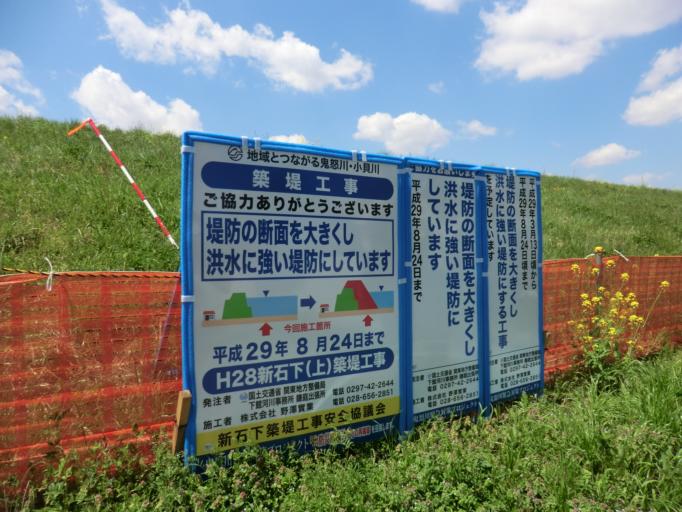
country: JP
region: Ibaraki
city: Ishige
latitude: 36.1086
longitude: 139.9697
